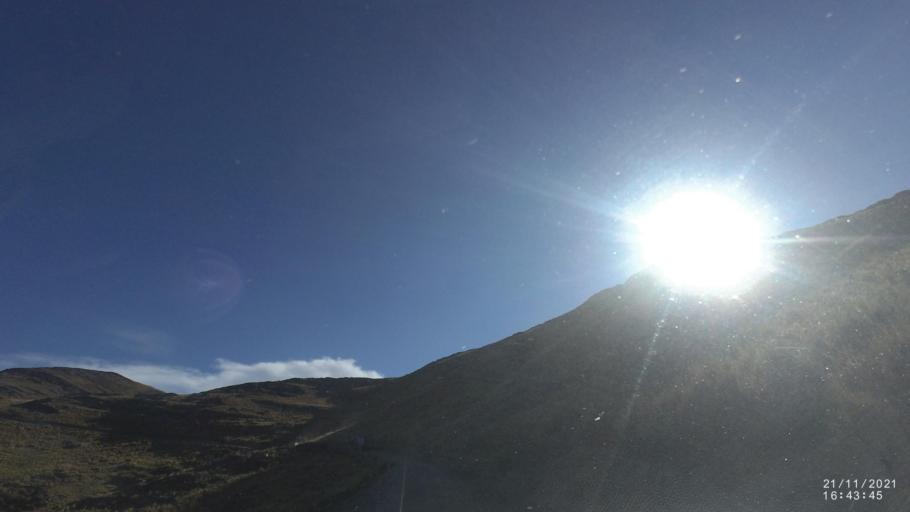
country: BO
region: Cochabamba
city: Cochabamba
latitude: -17.0716
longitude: -66.2576
